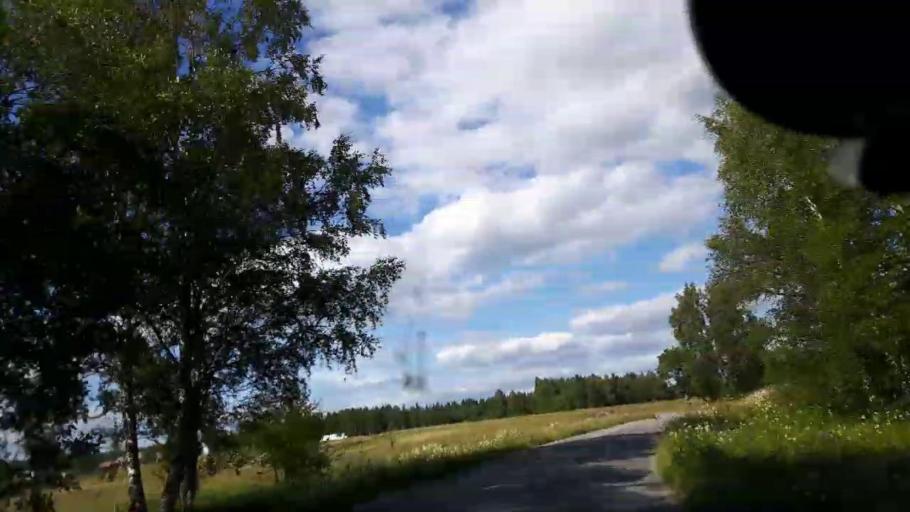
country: SE
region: Jaemtland
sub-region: Braecke Kommun
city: Braecke
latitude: 62.8510
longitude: 15.2952
